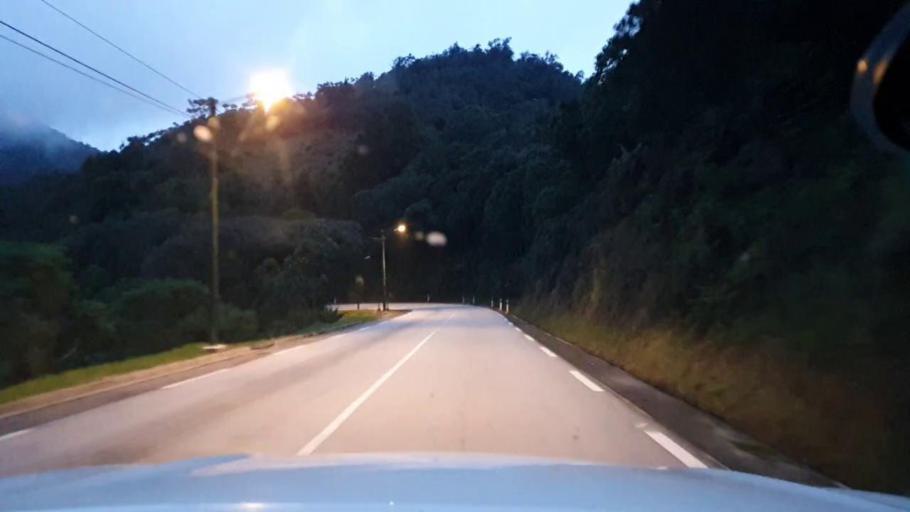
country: RW
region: Southern Province
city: Nzega
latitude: -2.5263
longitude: 29.3798
